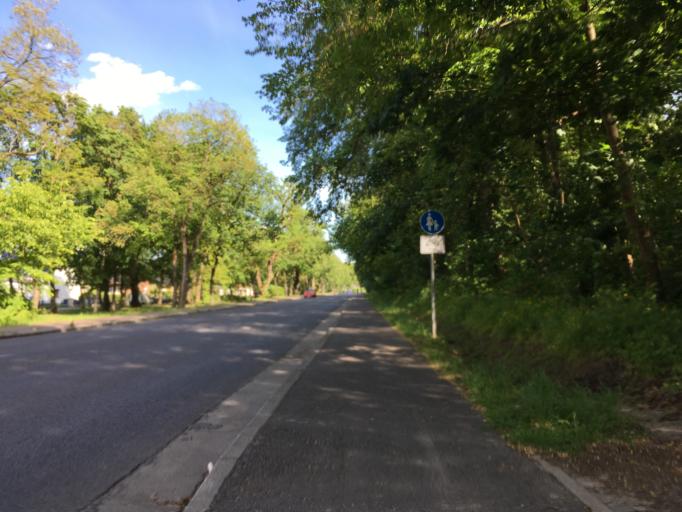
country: DE
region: Brandenburg
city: Wriezen
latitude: 52.7274
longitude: 14.1219
